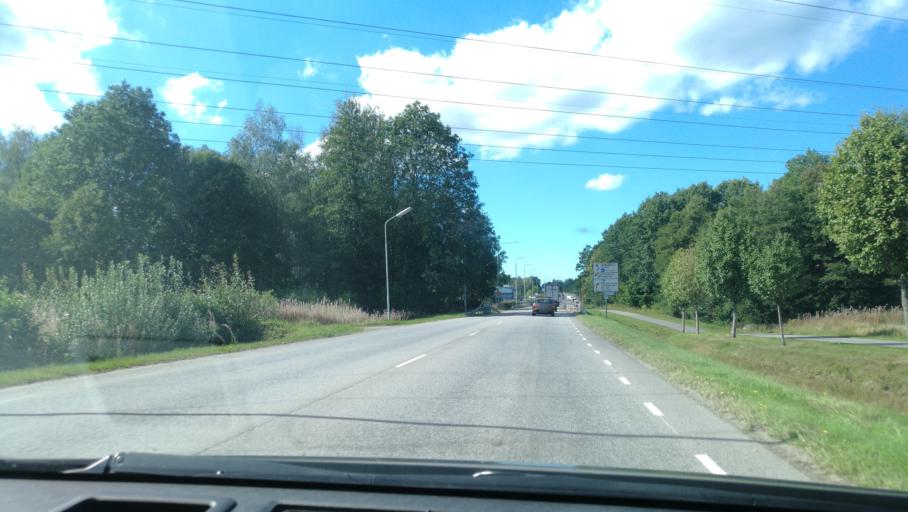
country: SE
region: Vaestra Goetaland
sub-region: Mariestads Kommun
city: Mariestad
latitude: 58.6921
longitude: 13.8277
